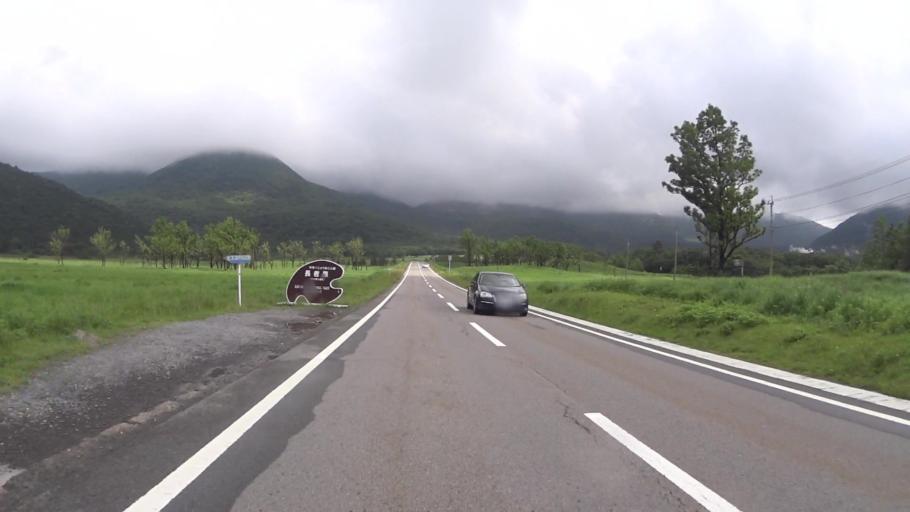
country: JP
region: Oita
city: Tsukawaki
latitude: 33.1239
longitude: 131.2296
